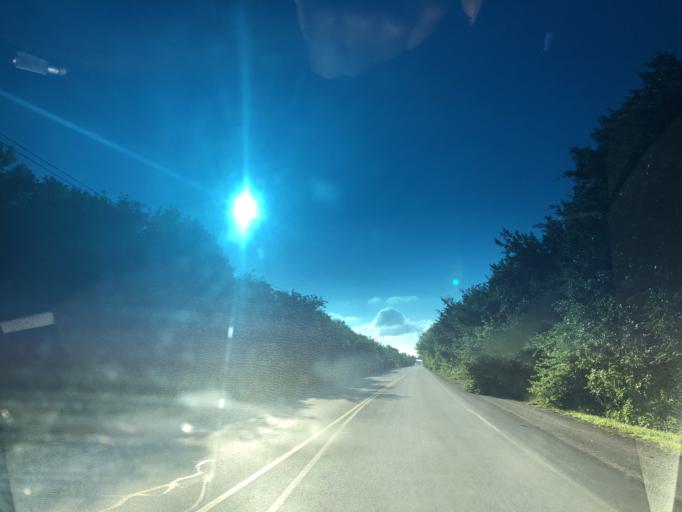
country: US
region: Texas
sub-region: Dallas County
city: Grand Prairie
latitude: 32.7778
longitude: -97.0054
